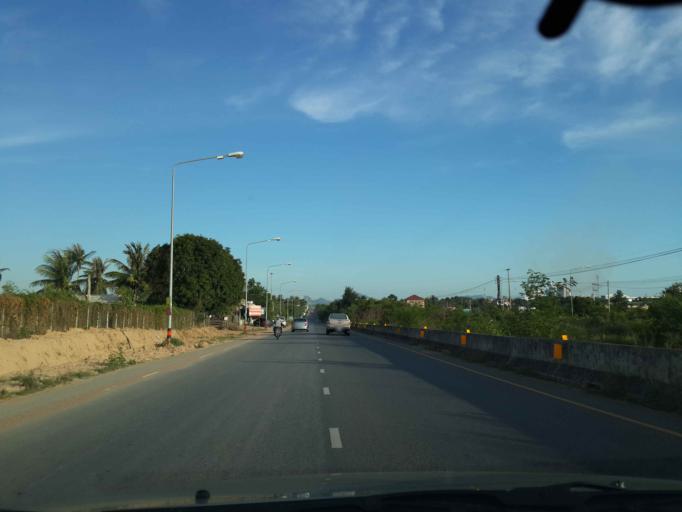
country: TH
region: Chon Buri
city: Phatthaya
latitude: 12.8737
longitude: 100.9082
